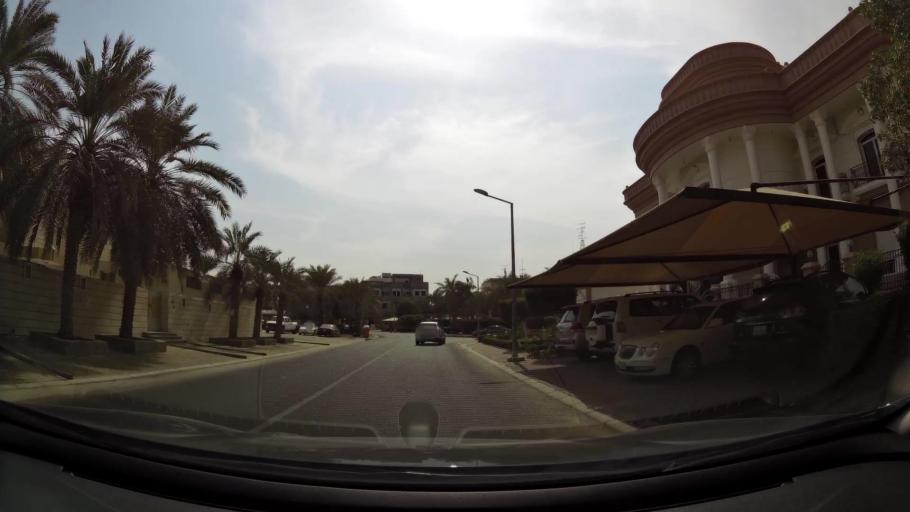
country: KW
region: Al Asimah
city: Ash Shamiyah
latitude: 29.3470
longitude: 47.9749
